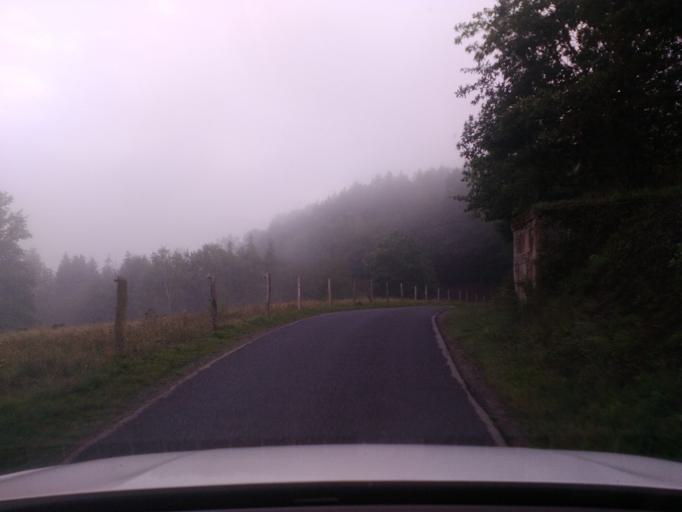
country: FR
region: Lorraine
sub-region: Departement des Vosges
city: Moyenmoutier
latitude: 48.3830
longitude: 6.9041
